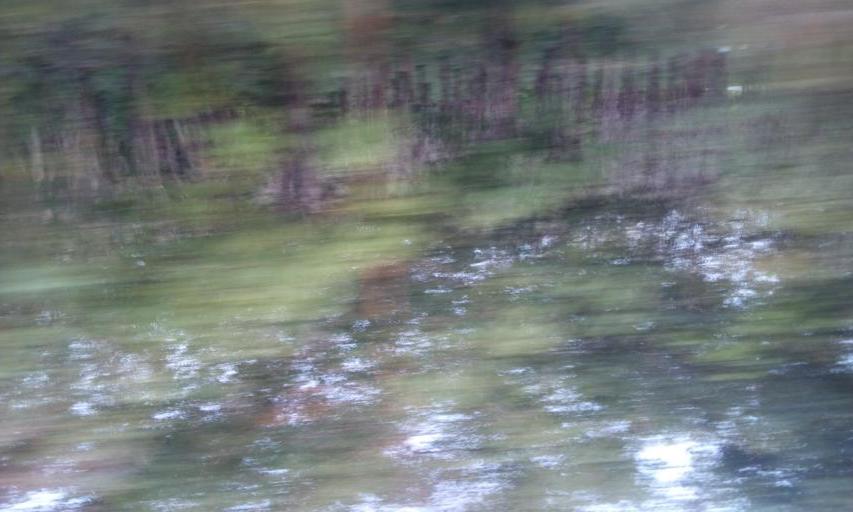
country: TH
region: Trat
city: Laem Ngop
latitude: 12.1902
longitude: 102.2956
